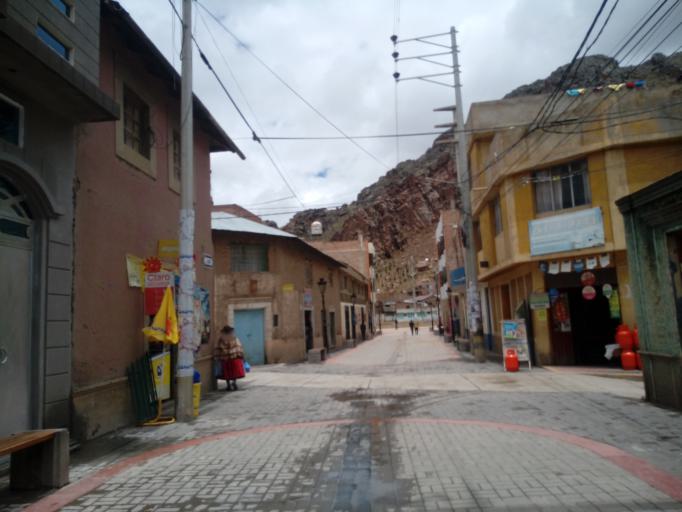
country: PE
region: Puno
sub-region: San Antonio De Putina
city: Putina
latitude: -14.9151
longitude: -69.8679
